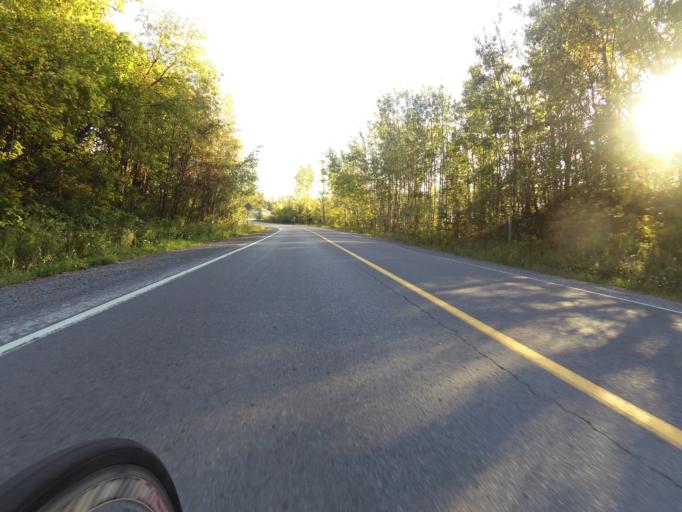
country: CA
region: Ontario
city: Bells Corners
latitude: 45.2165
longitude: -75.7115
